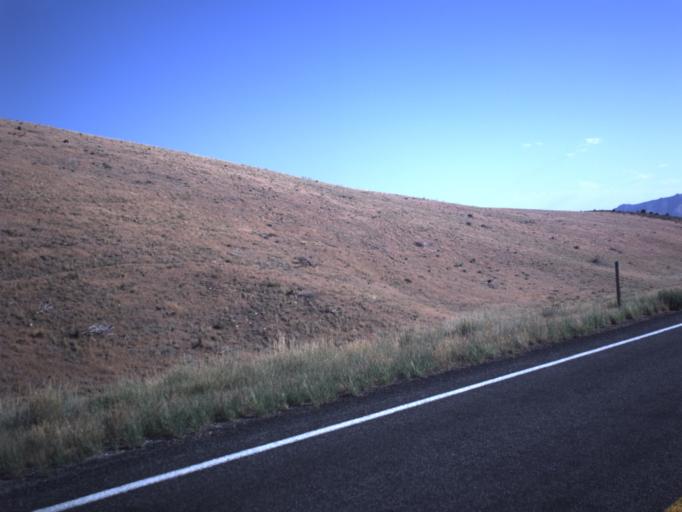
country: US
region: Utah
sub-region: Iron County
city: Parowan
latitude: 38.0855
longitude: -112.9555
